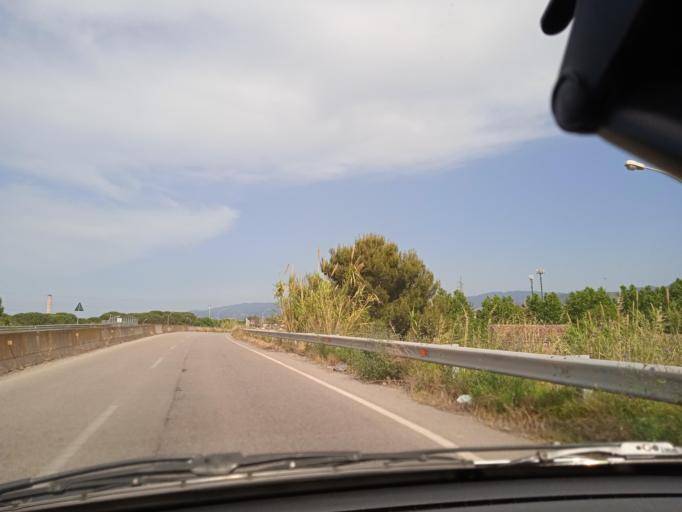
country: IT
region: Sicily
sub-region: Messina
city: Milazzo
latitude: 38.1971
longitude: 15.2512
